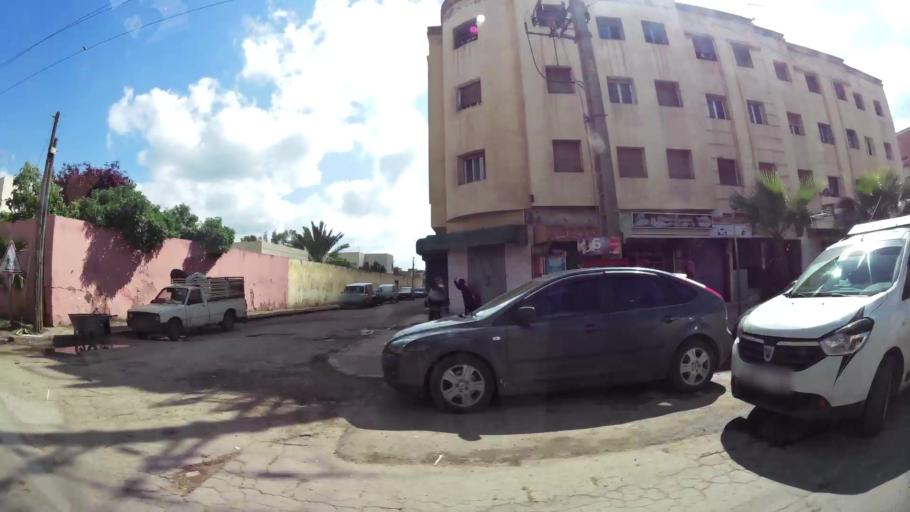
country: MA
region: Grand Casablanca
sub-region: Mediouna
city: Mediouna
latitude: 33.4519
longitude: -7.5126
